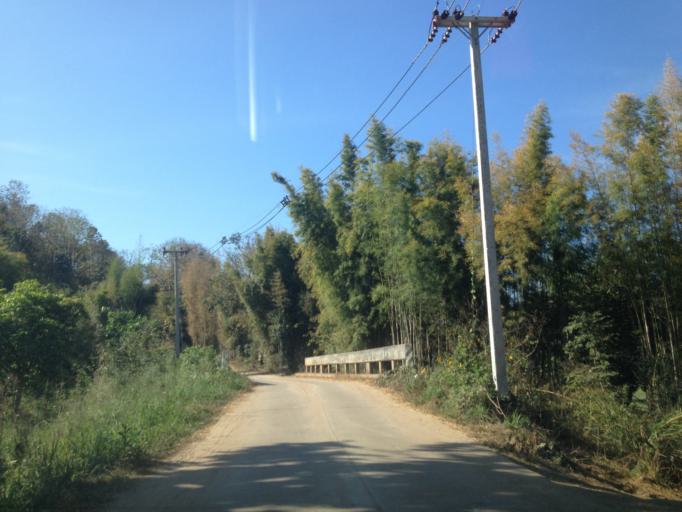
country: TH
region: Mae Hong Son
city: Ban Huai I Huak
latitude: 18.0804
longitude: 98.1909
